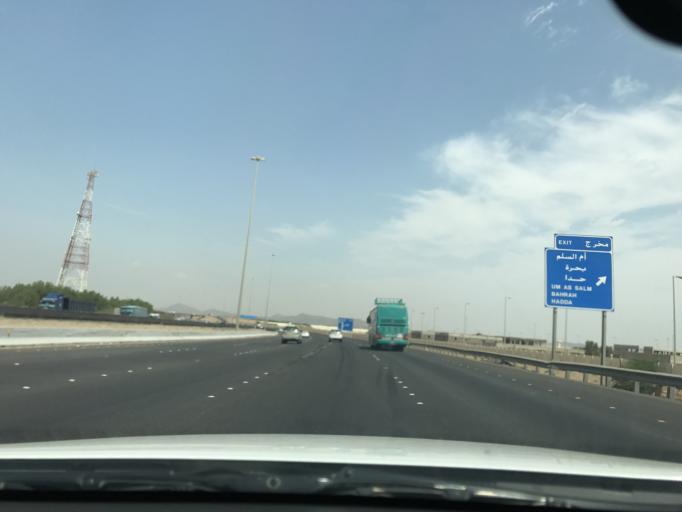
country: SA
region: Makkah
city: Jeddah
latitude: 21.3901
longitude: 39.4160
